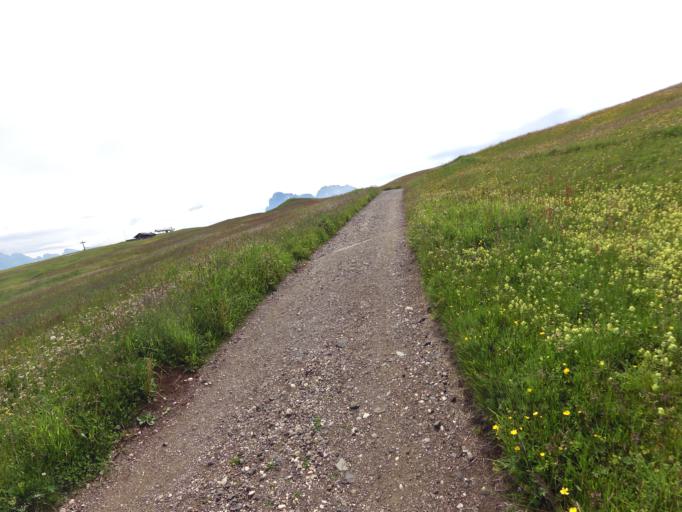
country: IT
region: Trentino-Alto Adige
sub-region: Bolzano
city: Siusi
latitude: 46.5261
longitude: 11.6140
